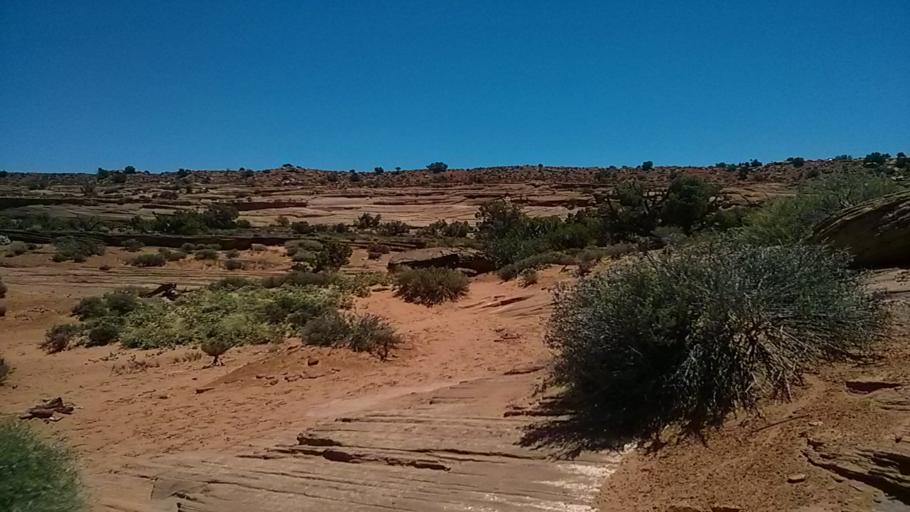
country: US
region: Arizona
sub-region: Coconino County
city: Page
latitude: 37.4790
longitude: -111.2204
